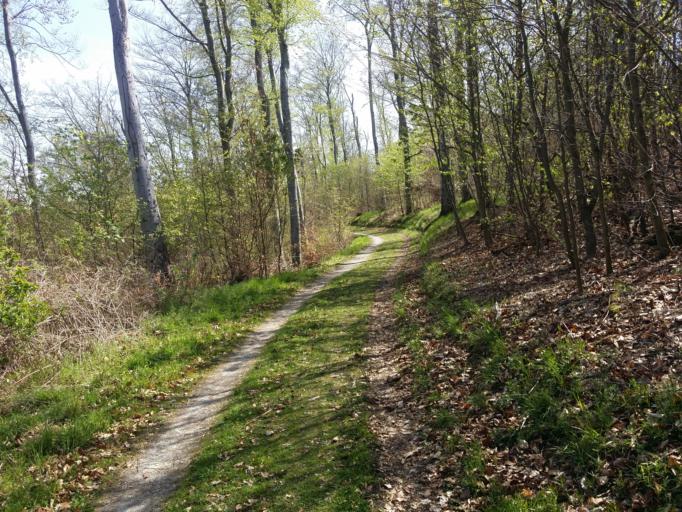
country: DE
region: Saxony-Anhalt
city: Gernrode
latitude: 51.7182
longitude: 11.1351
